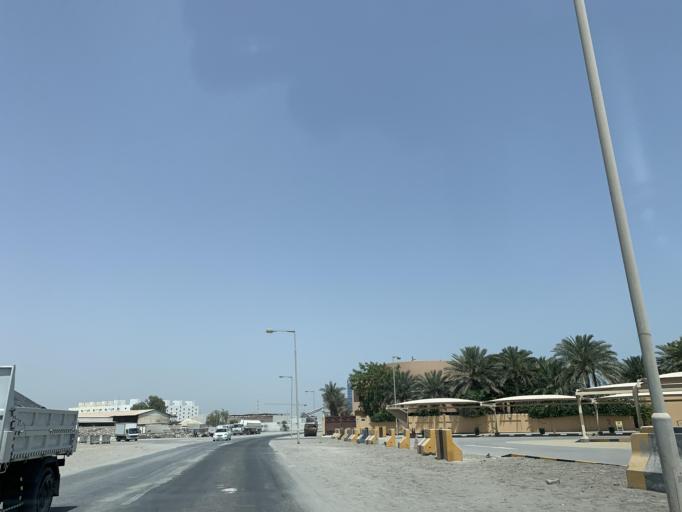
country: BH
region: Northern
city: Sitrah
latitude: 26.1448
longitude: 50.6010
